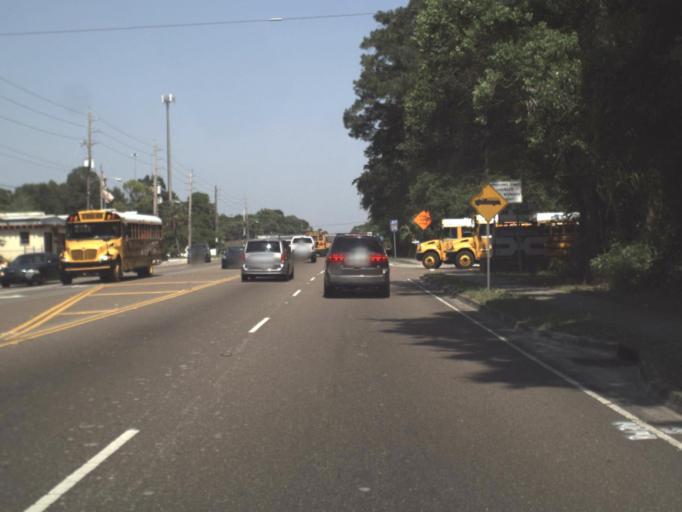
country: US
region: Florida
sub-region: Clay County
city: Bellair-Meadowbrook Terrace
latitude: 30.2697
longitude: -81.7716
